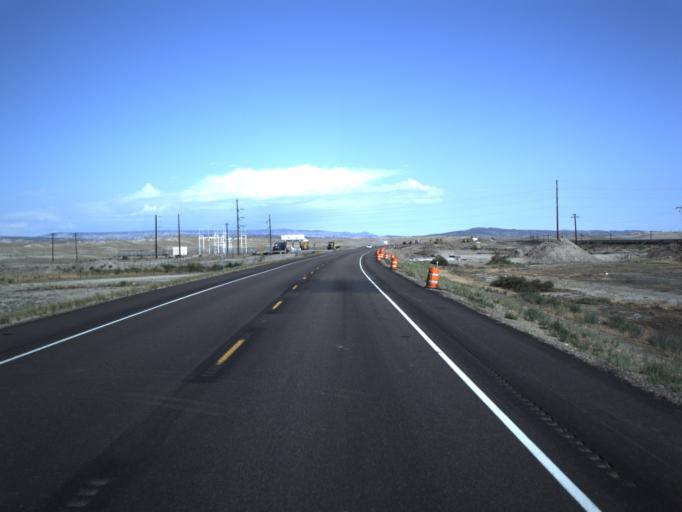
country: US
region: Utah
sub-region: Carbon County
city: East Carbon City
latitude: 39.0236
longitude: -110.2973
